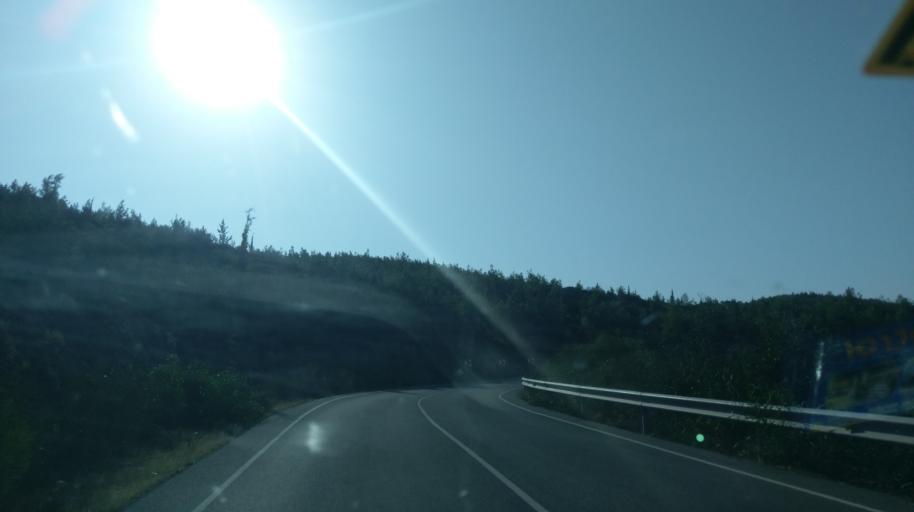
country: CY
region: Lefkosia
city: Kato Pyrgos
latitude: 35.1716
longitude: 32.7248
